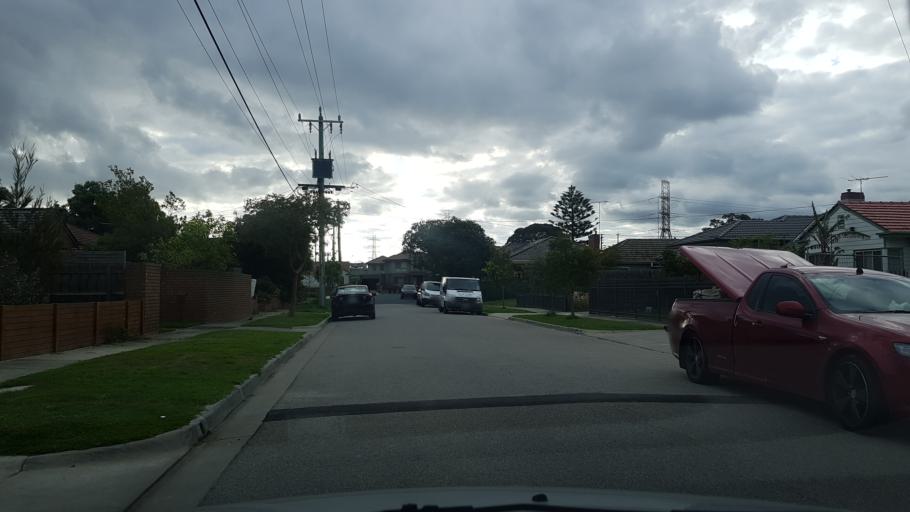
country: AU
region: Victoria
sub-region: Greater Dandenong
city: Springvale
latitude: -37.9410
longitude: 145.1467
